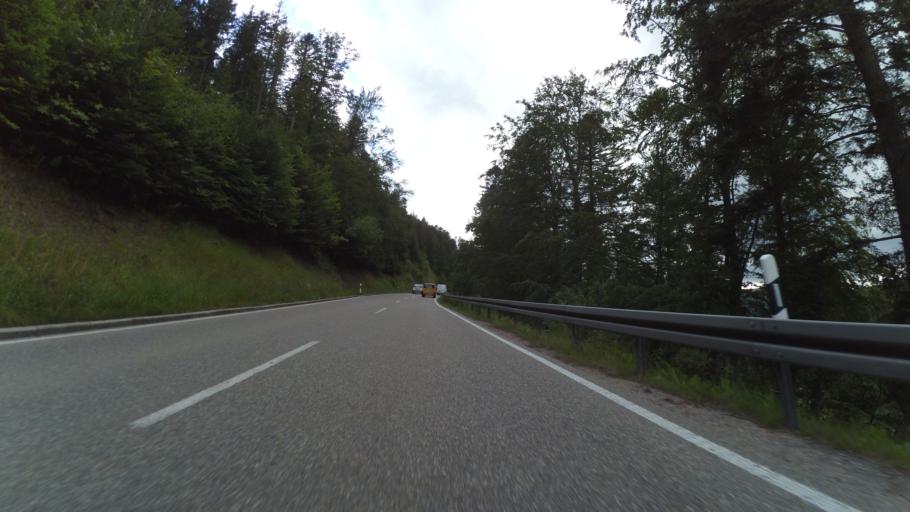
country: DE
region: Baden-Wuerttemberg
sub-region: Freiburg Region
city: Hinterzarten
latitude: 47.8792
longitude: 8.1188
